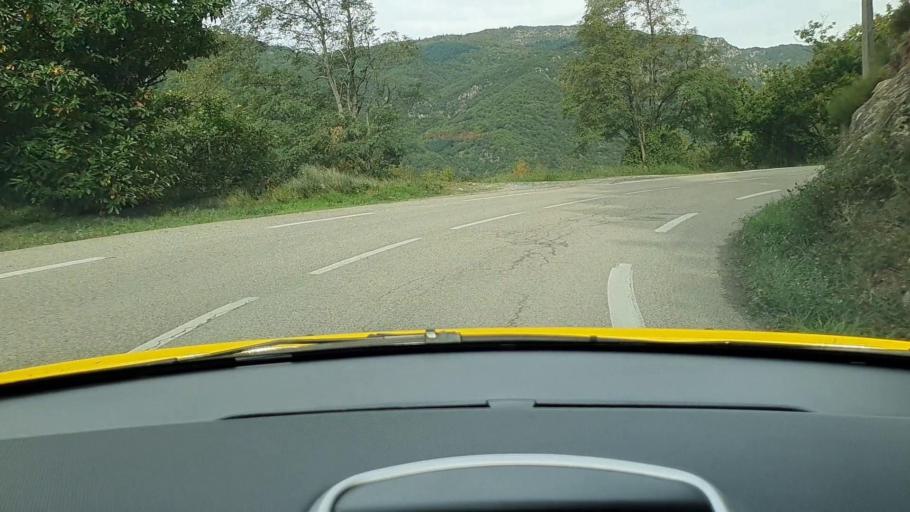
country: FR
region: Languedoc-Roussillon
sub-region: Departement du Gard
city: Le Vigan
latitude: 44.0224
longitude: 3.5967
